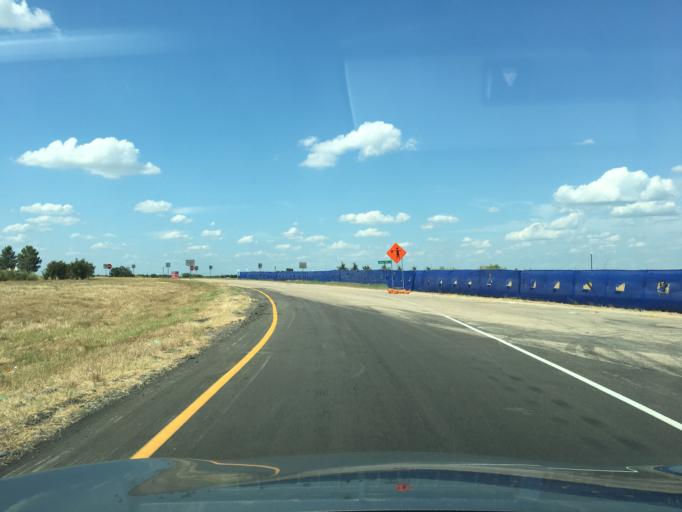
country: US
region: Texas
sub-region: Tarrant County
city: Mansfield
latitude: 32.5363
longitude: -97.1013
